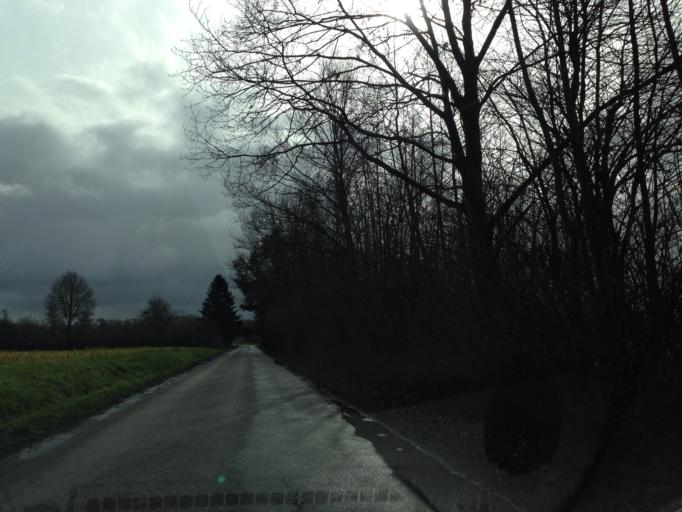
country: DE
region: North Rhine-Westphalia
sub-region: Regierungsbezirk Munster
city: Muenster
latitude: 52.0100
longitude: 7.5904
